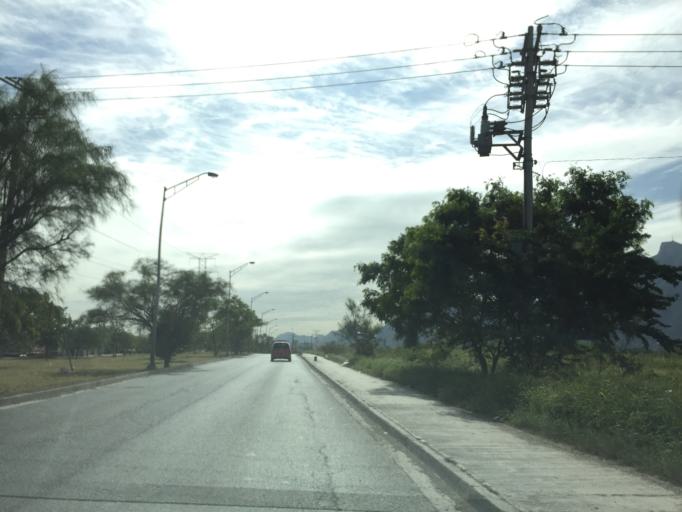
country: MX
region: Nuevo Leon
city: Guadalupe
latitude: 25.6993
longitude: -100.2140
